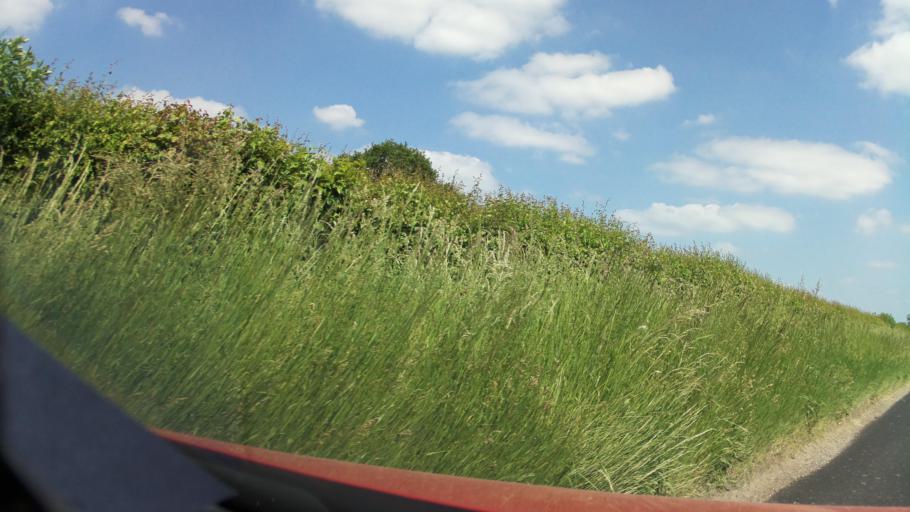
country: GB
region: England
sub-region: Wiltshire
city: Huish
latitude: 51.3600
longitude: -1.8137
